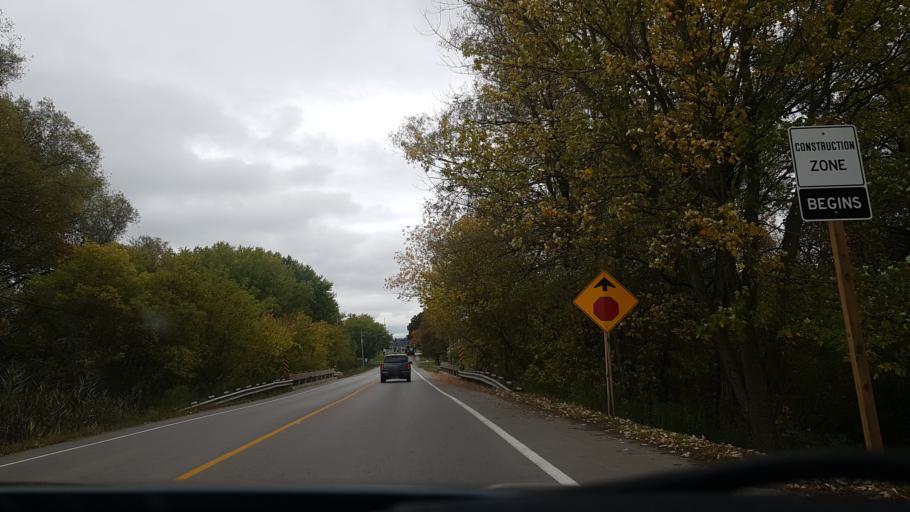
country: CA
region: Ontario
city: Omemee
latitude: 44.2027
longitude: -78.4699
